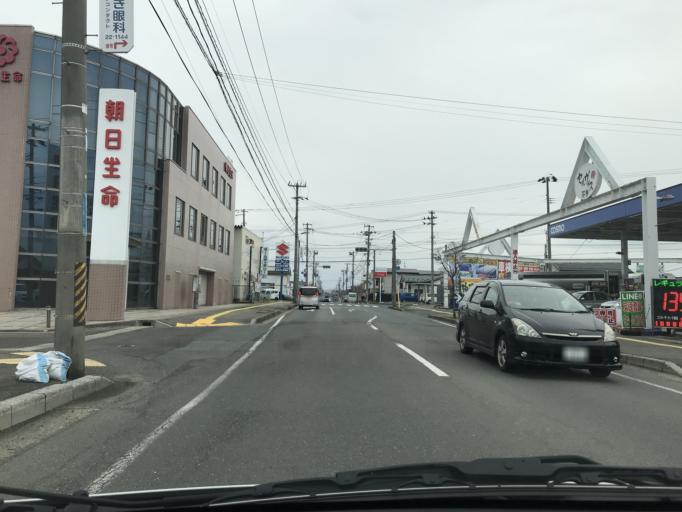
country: JP
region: Iwate
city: Hanamaki
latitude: 39.4007
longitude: 141.1056
